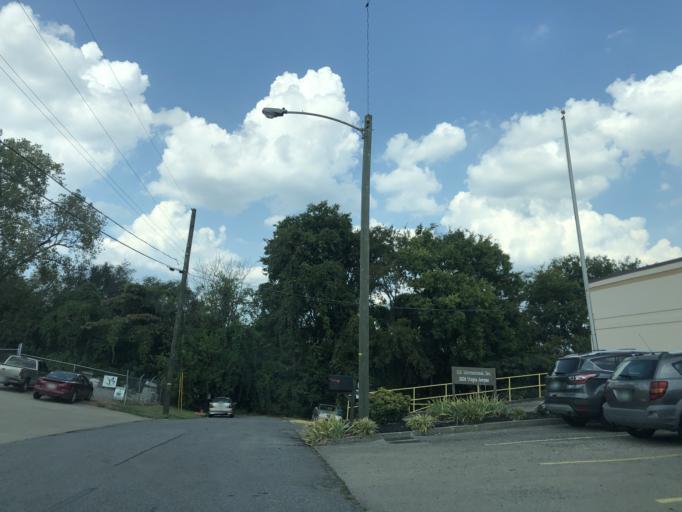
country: US
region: Tennessee
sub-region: Davidson County
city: Nashville
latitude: 36.1291
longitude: -86.7565
